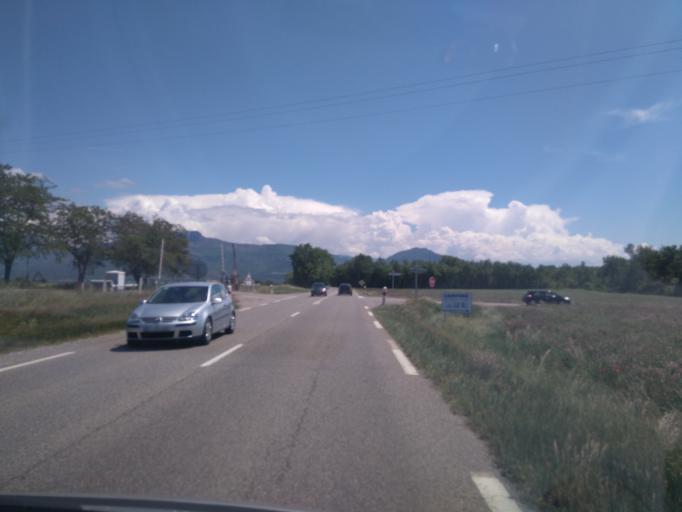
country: FR
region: Provence-Alpes-Cote d'Azur
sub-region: Departement des Hautes-Alpes
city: Laragne-Monteglin
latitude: 44.2538
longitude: 5.8753
